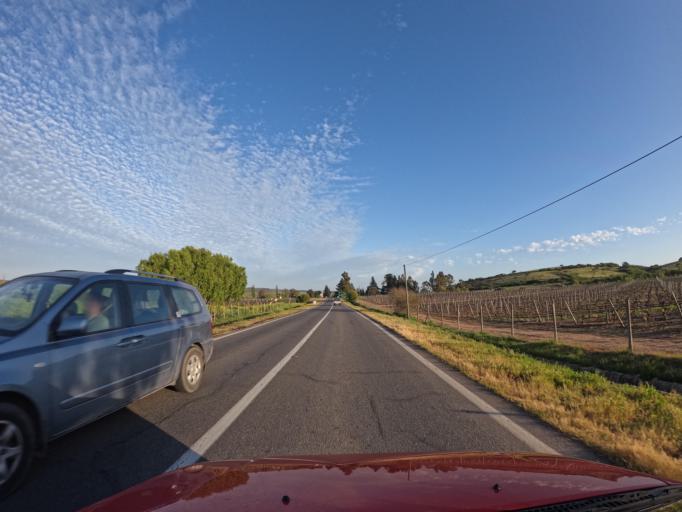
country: CL
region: O'Higgins
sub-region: Provincia de Colchagua
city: Santa Cruz
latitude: -34.2138
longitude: -71.7249
